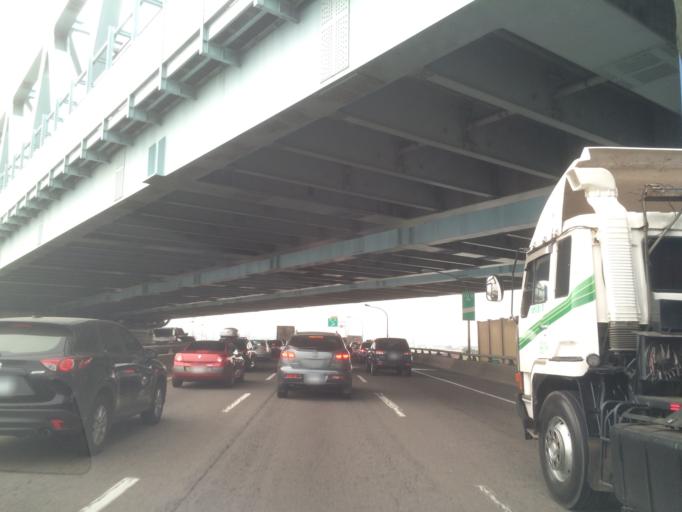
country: TW
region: Taiwan
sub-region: Changhua
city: Chang-hua
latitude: 24.1065
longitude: 120.6158
